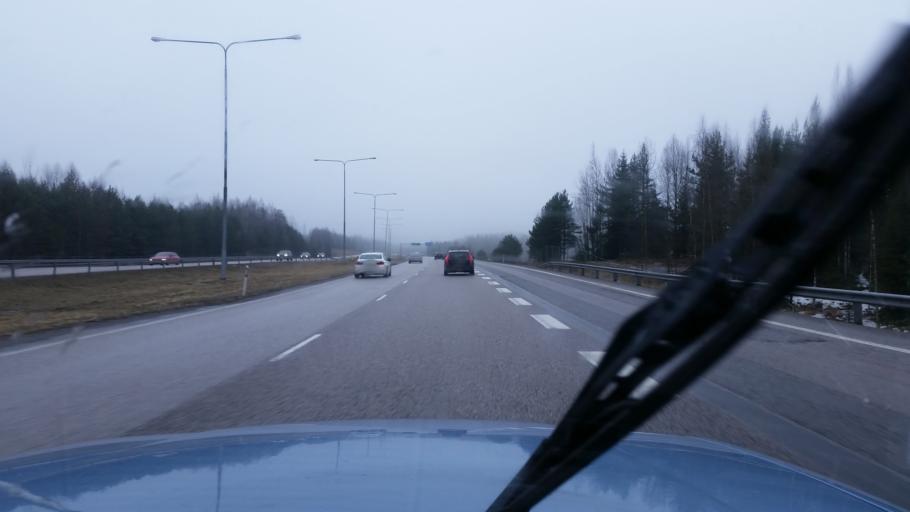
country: FI
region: Uusimaa
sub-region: Helsinki
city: Hyvinge
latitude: 60.5619
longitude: 24.8228
